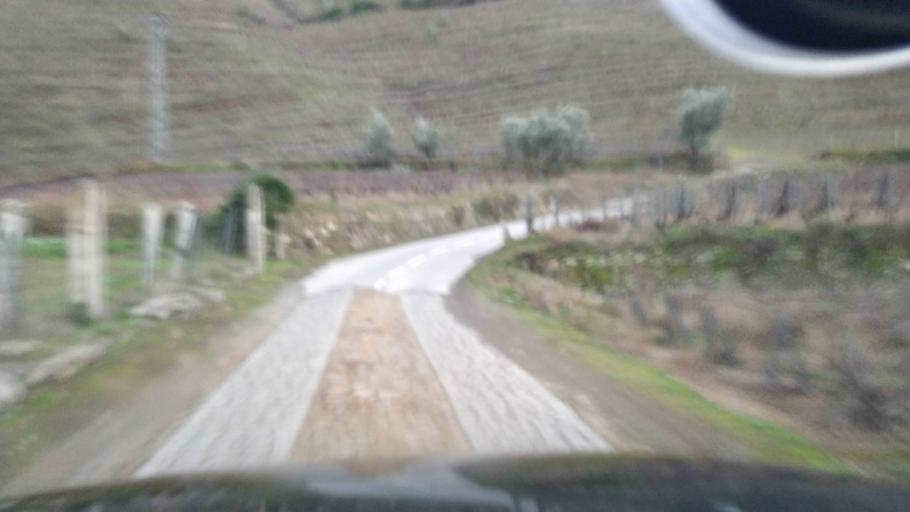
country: PT
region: Vila Real
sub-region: Santa Marta de Penaguiao
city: Santa Marta de Penaguiao
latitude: 41.2411
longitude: -7.7769
